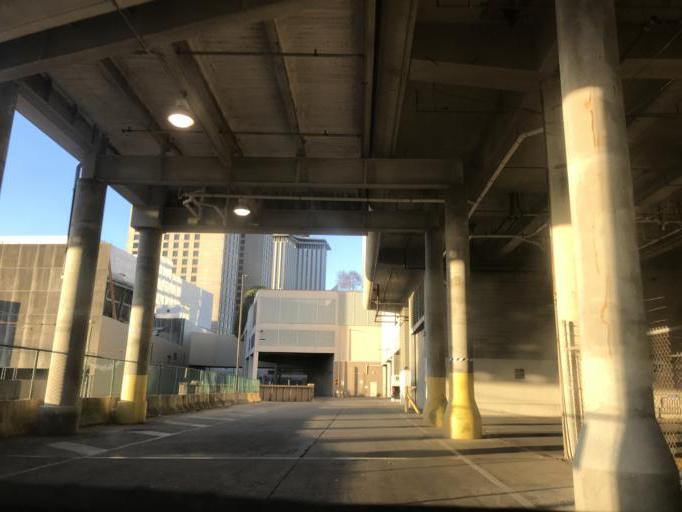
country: US
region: Louisiana
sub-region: Orleans Parish
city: New Orleans
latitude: 29.9452
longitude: -90.0624
